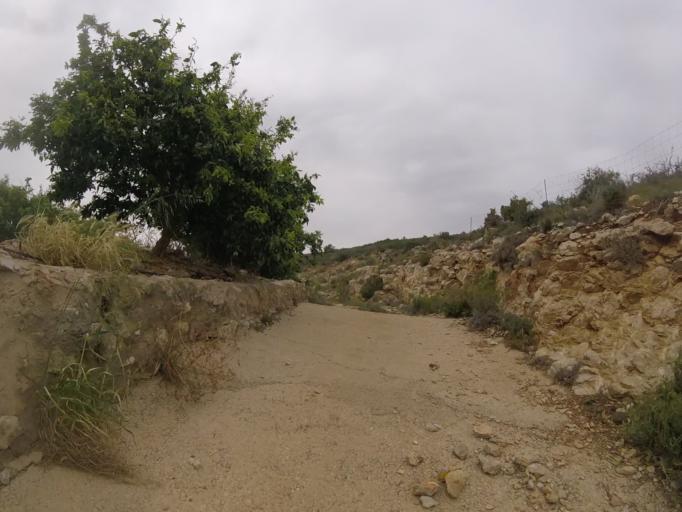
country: ES
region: Valencia
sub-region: Provincia de Castello
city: Alcala de Xivert
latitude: 40.2803
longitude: 0.2507
